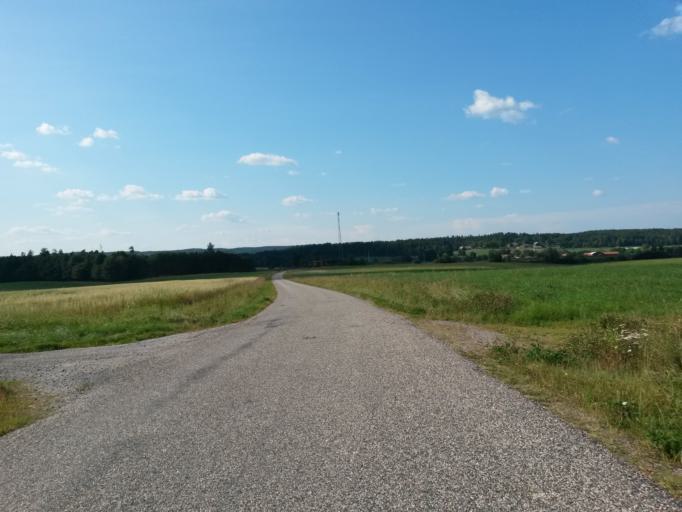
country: SE
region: Vaestra Goetaland
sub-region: Vargarda Kommun
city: Jonstorp
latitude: 57.9845
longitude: 12.6555
